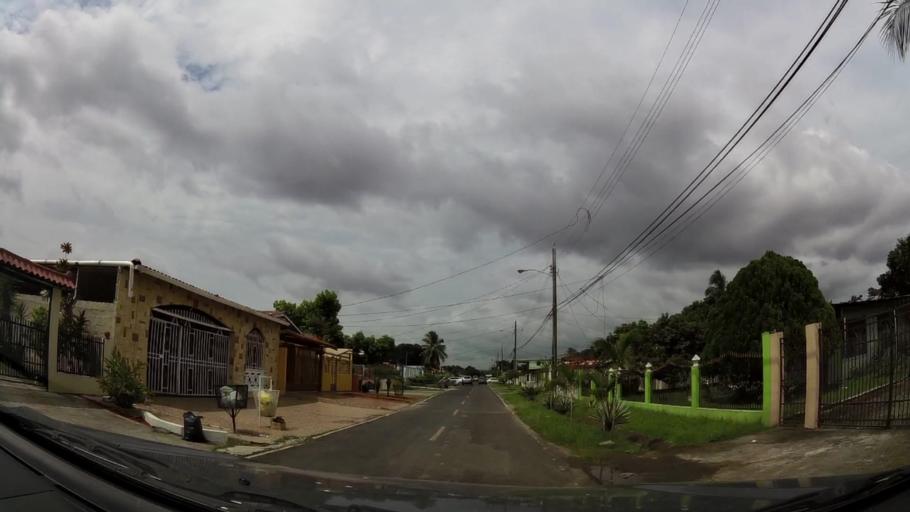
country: PA
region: Panama
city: San Miguelito
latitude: 9.0447
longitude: -79.4219
